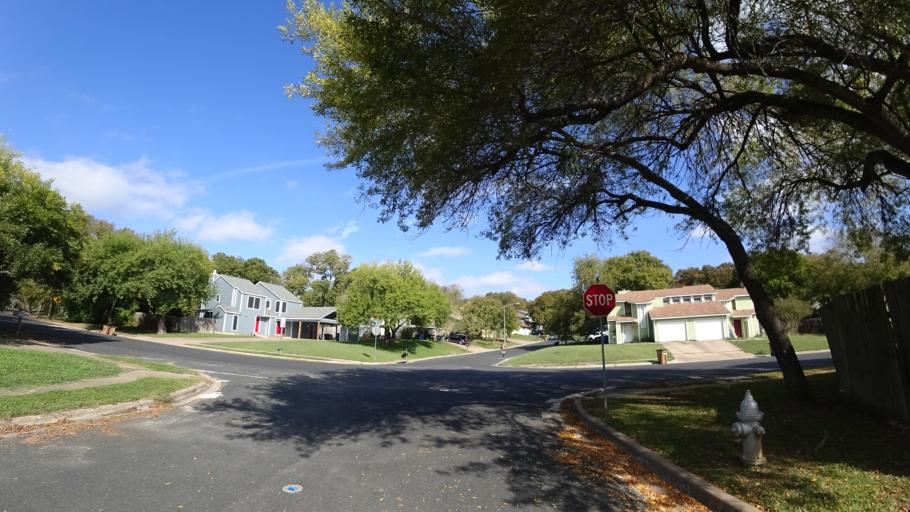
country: US
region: Texas
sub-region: Travis County
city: Manchaca
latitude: 30.1913
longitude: -97.8142
